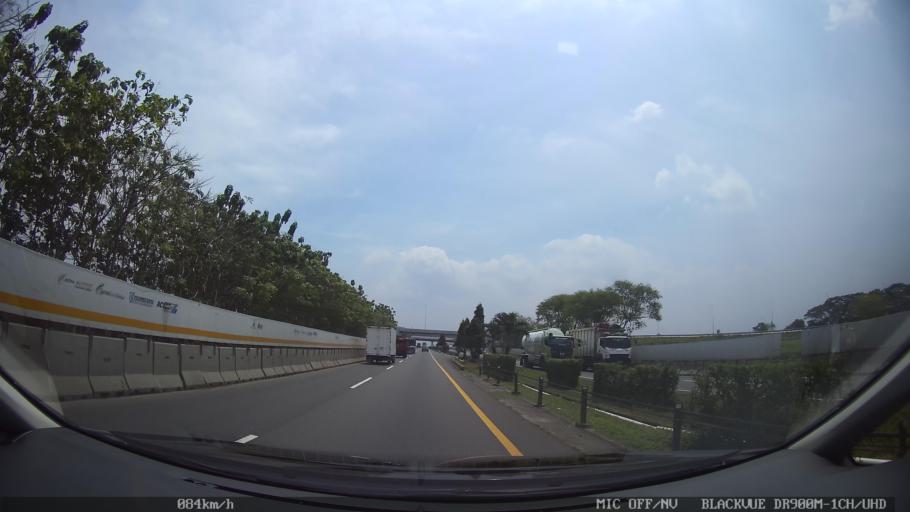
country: ID
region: Banten
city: Serang
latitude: -6.1386
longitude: 106.2470
